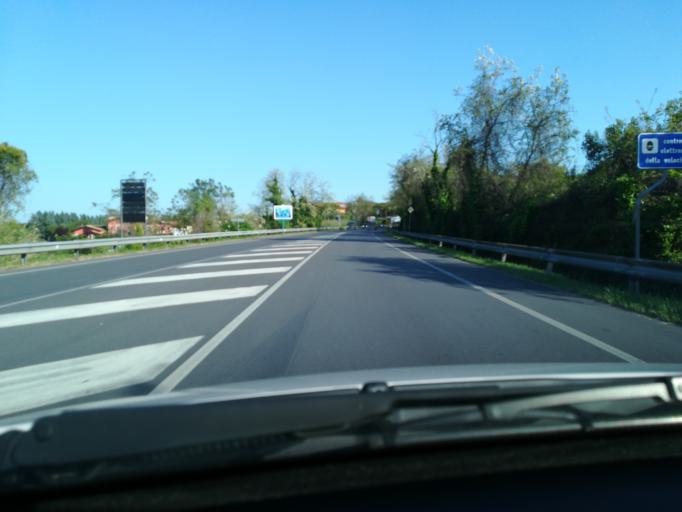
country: IT
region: Emilia-Romagna
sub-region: Provincia di Rimini
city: Montalbano
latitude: 43.9680
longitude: 12.7085
